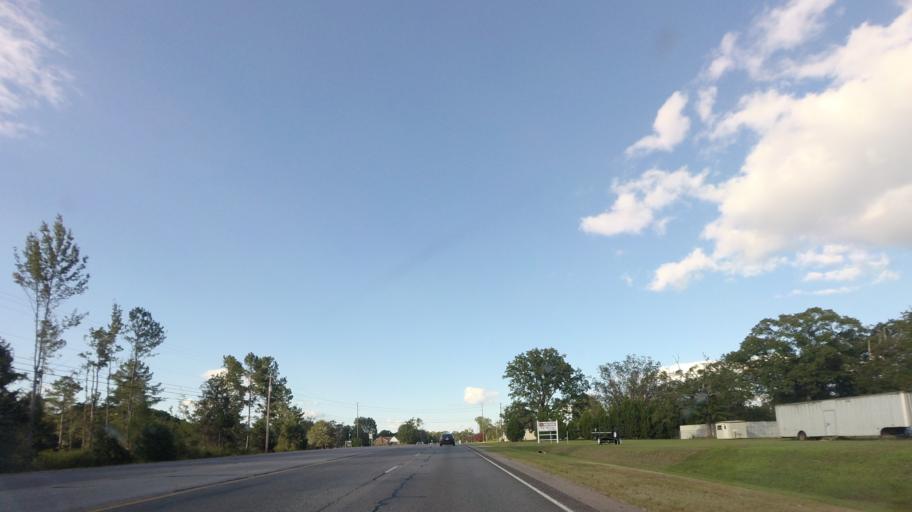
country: US
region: Georgia
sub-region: Upson County
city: Hannahs Mill
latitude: 32.9620
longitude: -84.3319
